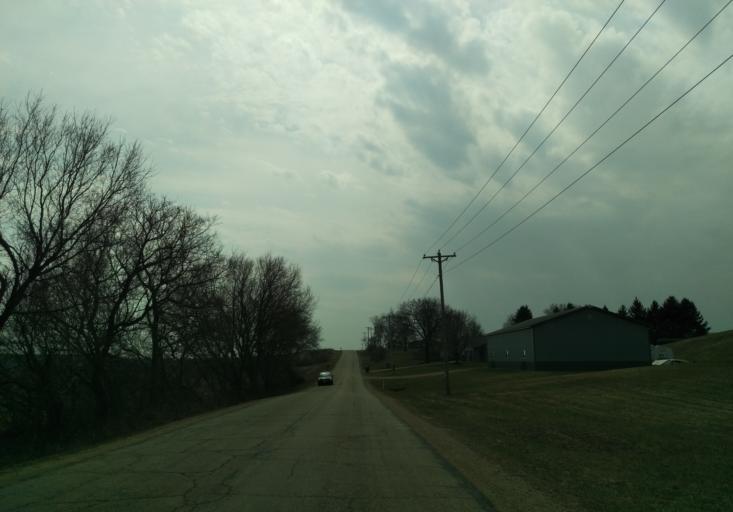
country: US
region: Wisconsin
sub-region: Dane County
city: Middleton
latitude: 43.1284
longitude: -89.4916
